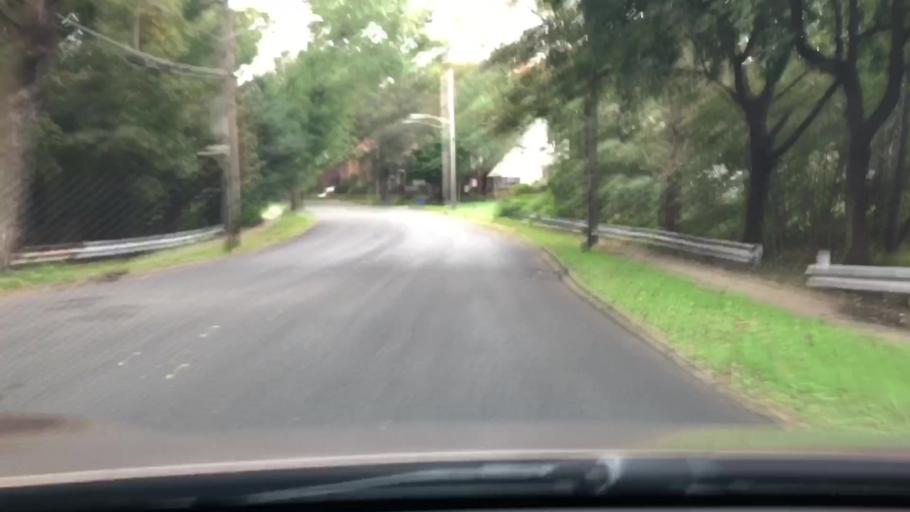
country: US
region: New York
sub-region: Westchester County
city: Bronxville
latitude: 40.9267
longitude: -73.8269
